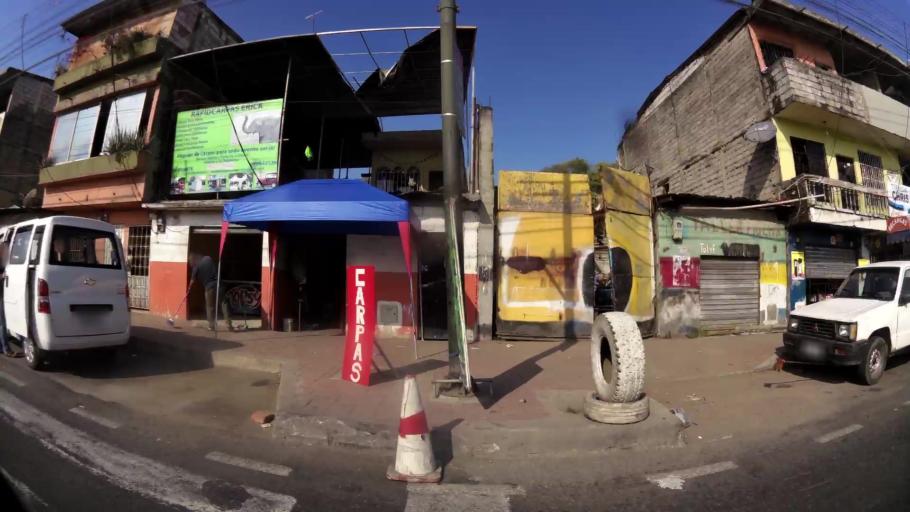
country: EC
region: Guayas
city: Eloy Alfaro
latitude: -2.1708
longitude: -79.8373
